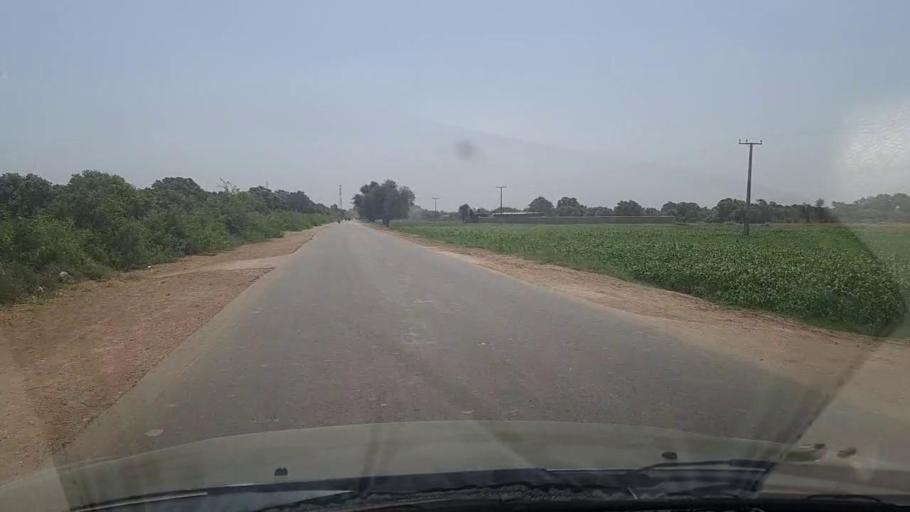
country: PK
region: Sindh
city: Tando Jam
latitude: 25.3611
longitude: 68.4931
